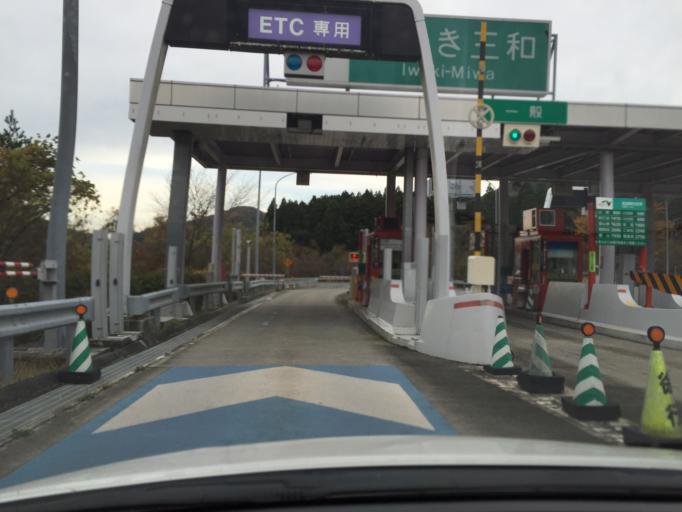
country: JP
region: Fukushima
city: Iwaki
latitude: 37.1017
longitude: 140.7713
